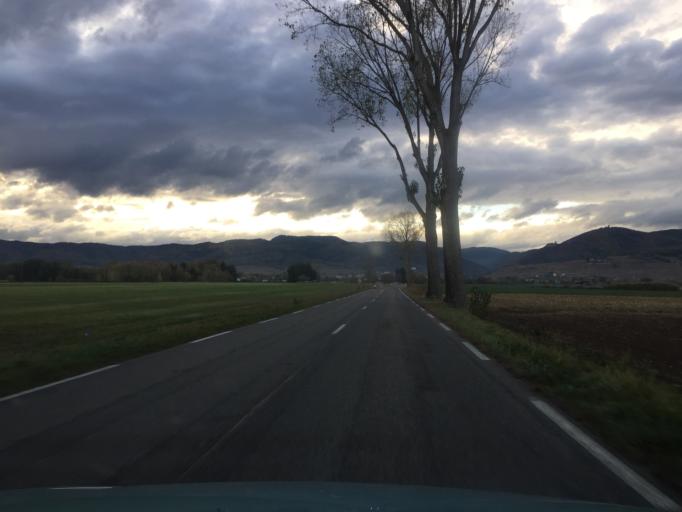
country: FR
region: Alsace
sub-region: Departement du Haut-Rhin
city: Bergheim
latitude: 48.1889
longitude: 7.3598
